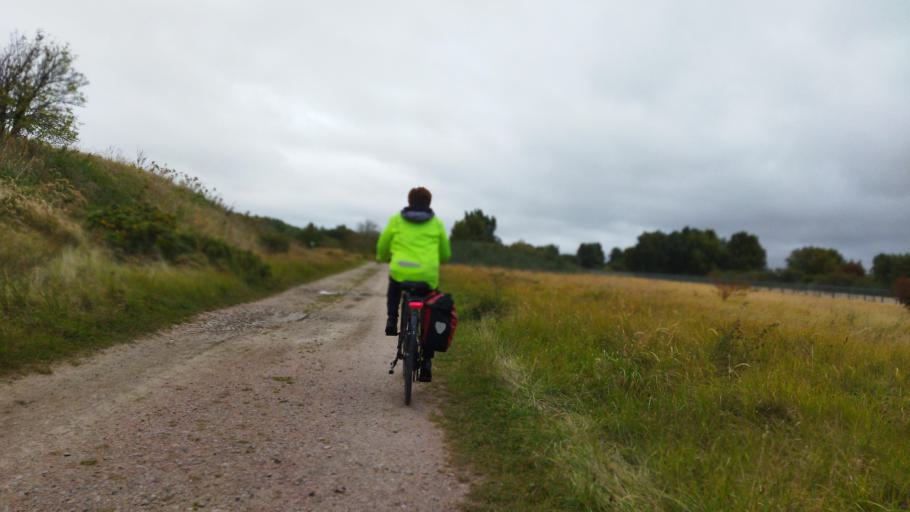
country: NL
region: Groningen
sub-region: Gemeente Delfzijl
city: Delfzijl
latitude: 53.3628
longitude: 7.0020
